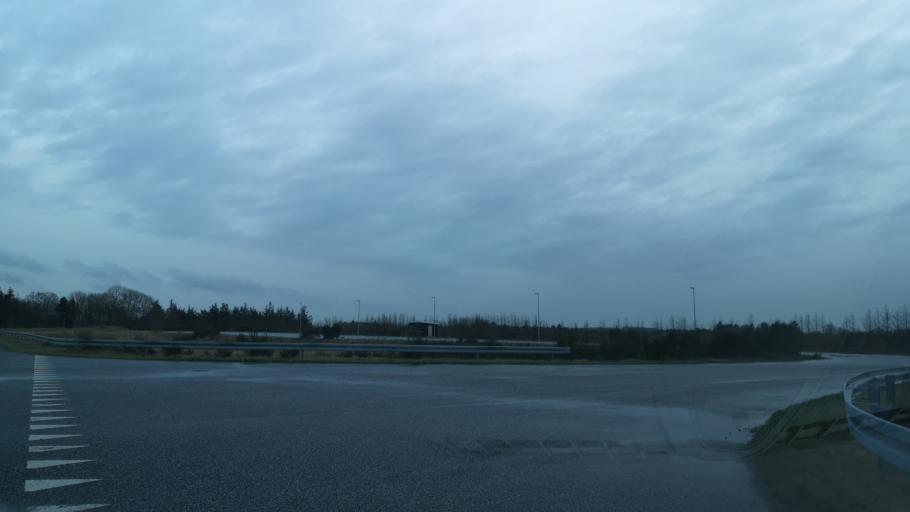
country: DK
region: Central Jutland
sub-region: Herning Kommune
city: Lind
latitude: 56.0133
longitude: 9.0306
